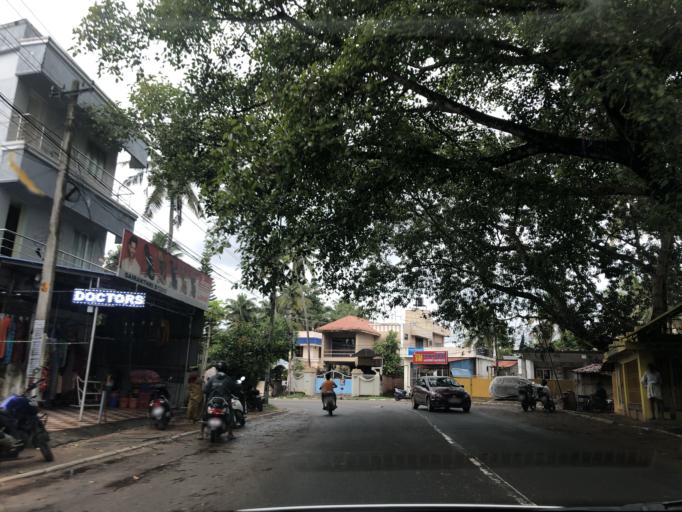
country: IN
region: Kerala
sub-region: Thiruvananthapuram
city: Thiruvananthapuram
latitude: 8.5114
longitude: 76.9077
